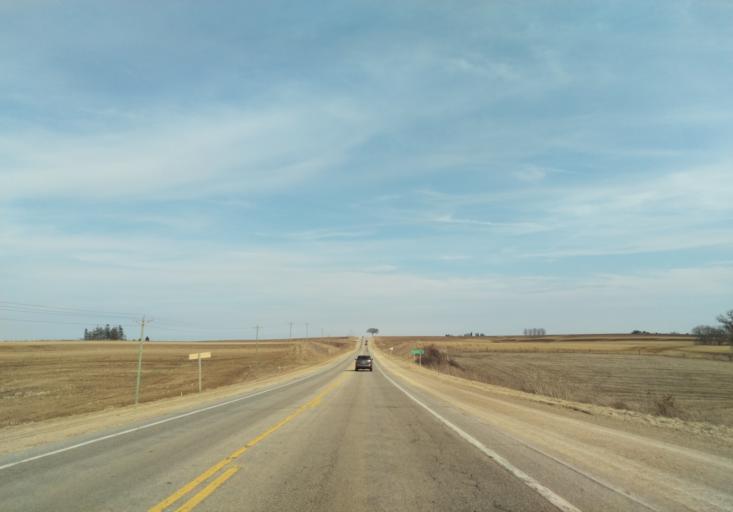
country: US
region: Wisconsin
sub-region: Grant County
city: Lancaster
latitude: 42.9742
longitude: -90.8577
